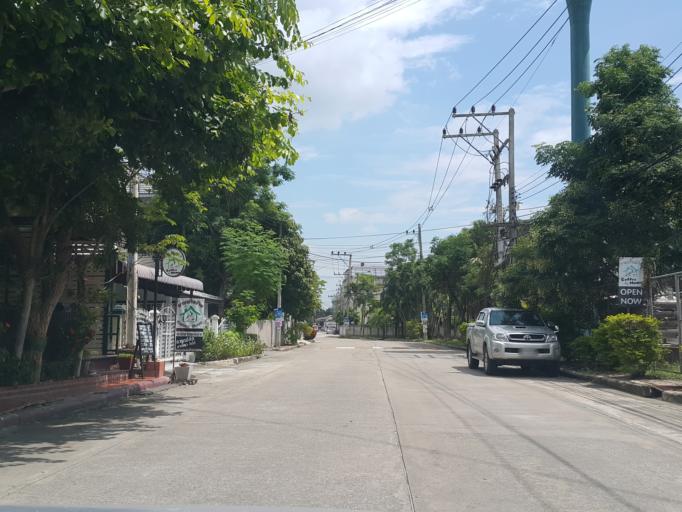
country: TH
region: Chiang Mai
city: Hang Dong
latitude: 18.7366
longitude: 98.9511
